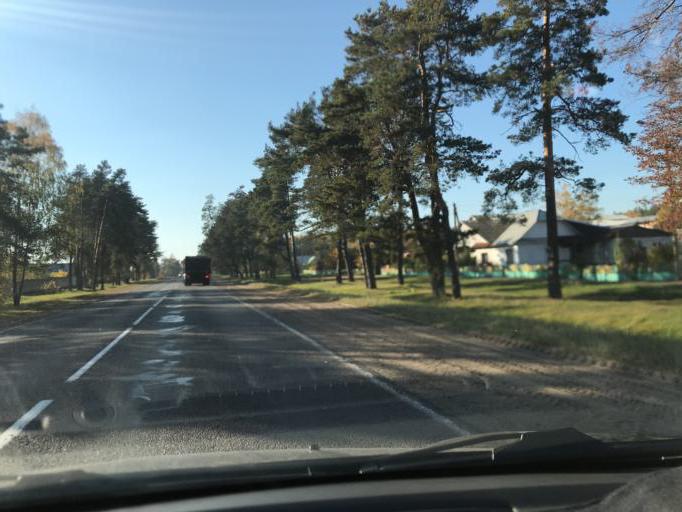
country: BY
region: Mogilev
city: Hlusha
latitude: 53.0872
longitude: 28.8544
